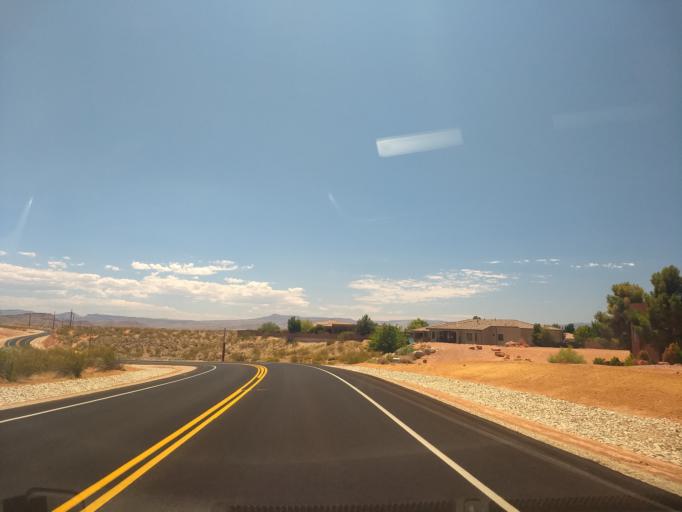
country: US
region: Utah
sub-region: Washington County
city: Washington
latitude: 37.1553
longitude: -113.5195
